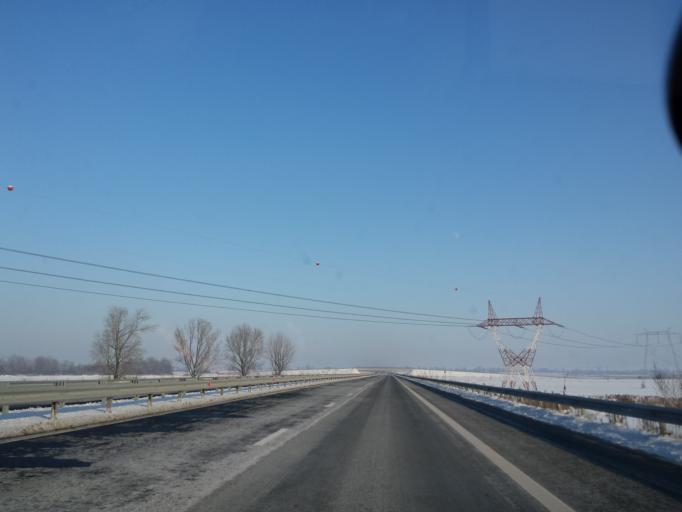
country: RO
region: Hunedoara
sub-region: Comuna Geoagiu
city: Geoagiu
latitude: 45.8805
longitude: 23.2094
